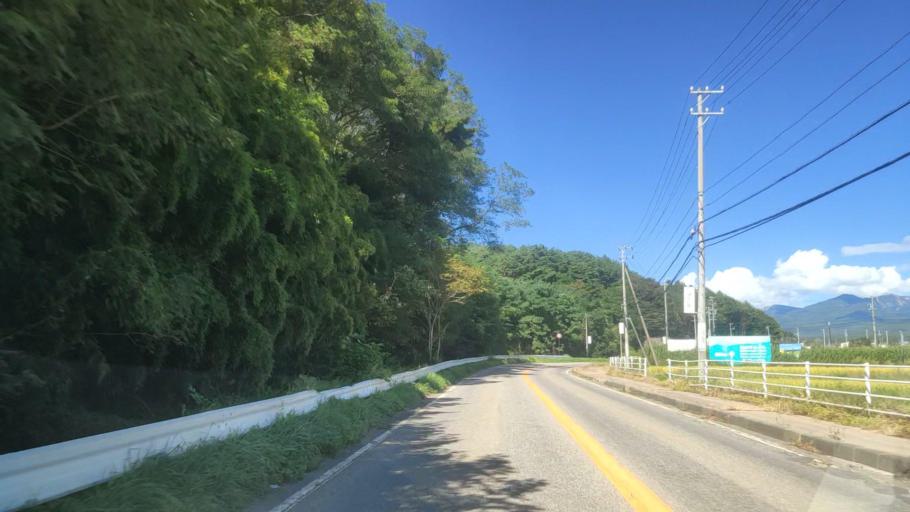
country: JP
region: Nagano
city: Chino
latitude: 35.9383
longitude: 138.2191
